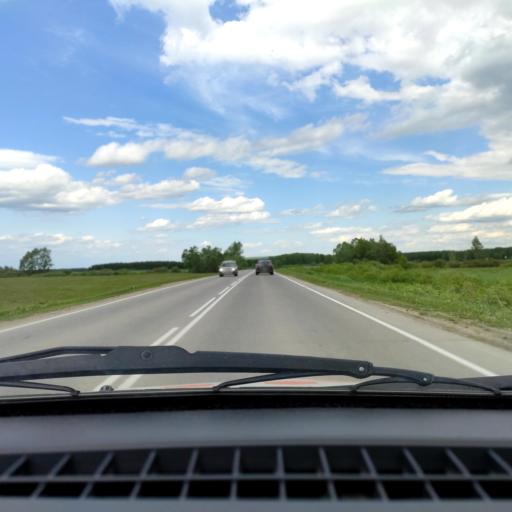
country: RU
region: Bashkortostan
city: Iglino
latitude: 54.9657
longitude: 56.4866
